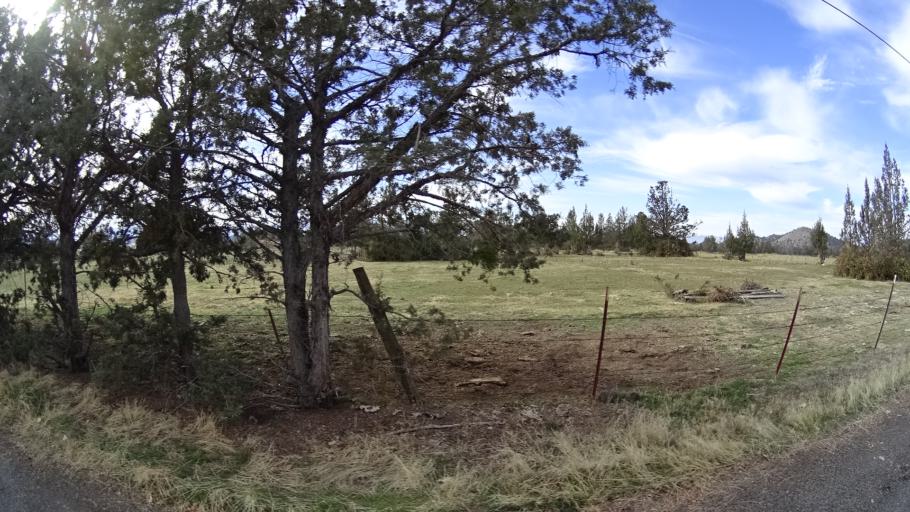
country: US
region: California
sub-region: Siskiyou County
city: Montague
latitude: 41.6395
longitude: -122.4190
